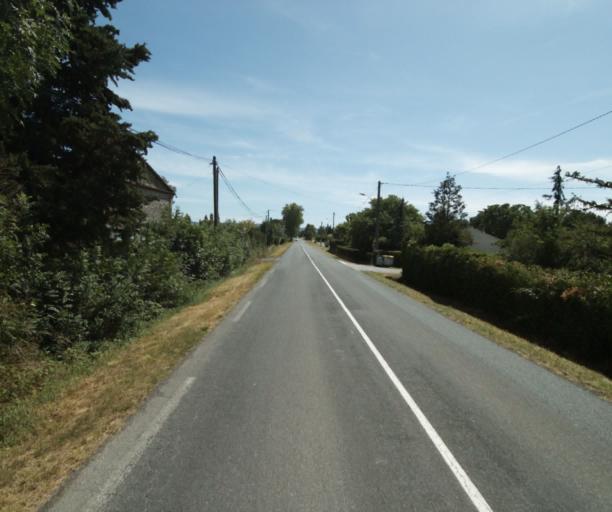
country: FR
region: Midi-Pyrenees
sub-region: Departement du Tarn
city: Puylaurens
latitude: 43.5179
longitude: 2.0097
